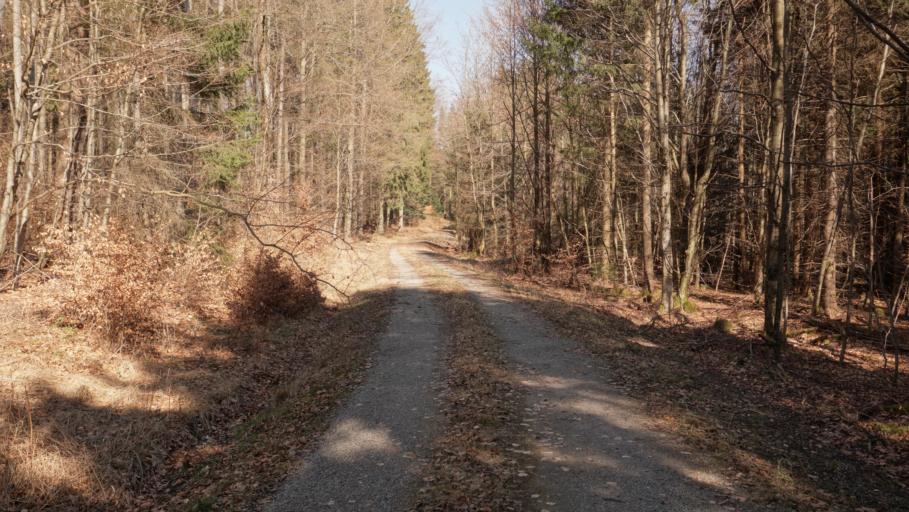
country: DE
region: Baden-Wuerttemberg
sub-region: Karlsruhe Region
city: Fahrenbach
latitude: 49.4464
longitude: 9.1368
